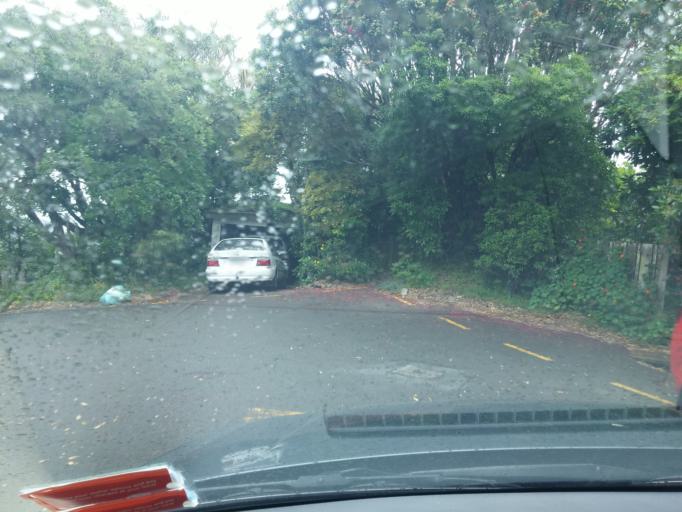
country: NZ
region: Wellington
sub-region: Wellington City
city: Kelburn
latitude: -41.2863
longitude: 174.7557
